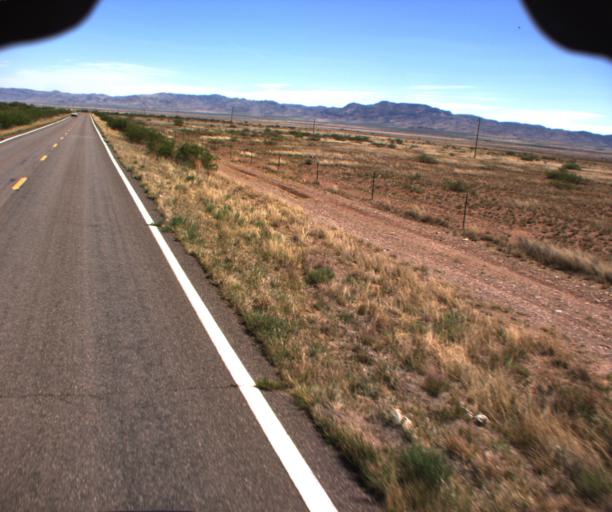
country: US
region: Arizona
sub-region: Cochise County
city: Douglas
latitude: 31.6469
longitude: -109.1673
